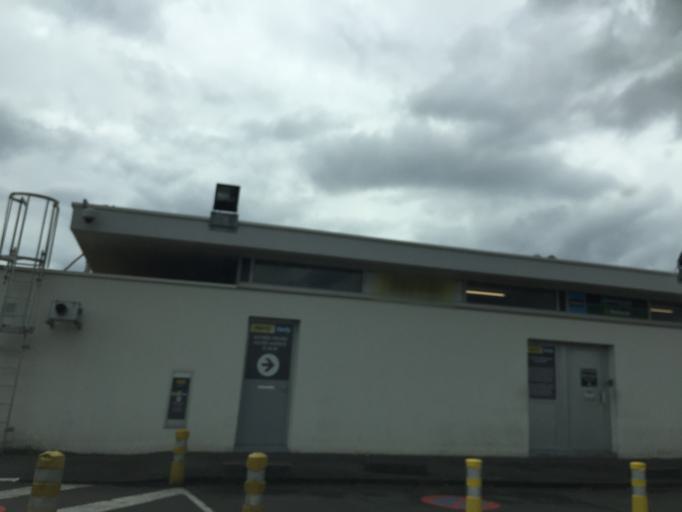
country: FR
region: Pays de la Loire
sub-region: Departement de la Loire-Atlantique
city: Bouguenais
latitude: 47.1582
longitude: -1.6006
